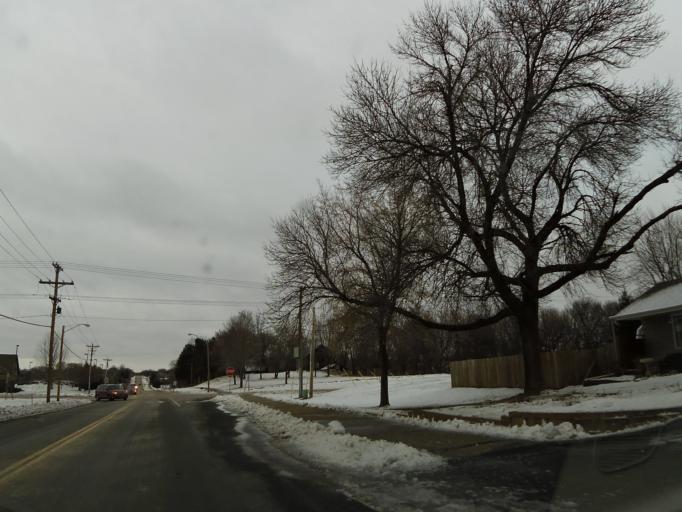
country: US
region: Minnesota
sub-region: Carver County
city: Chaska
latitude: 44.8050
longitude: -93.6120
